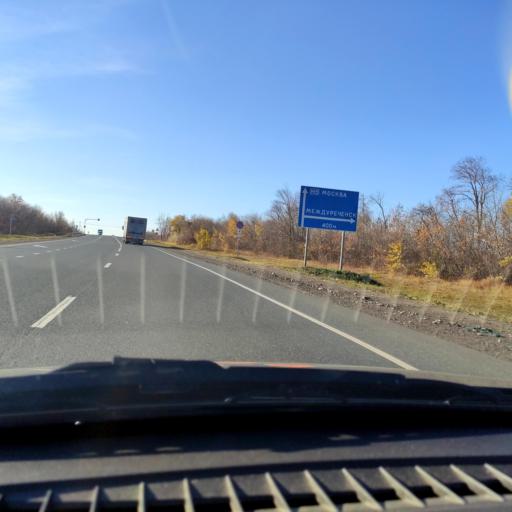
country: RU
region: Samara
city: Mezhdurechensk
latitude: 53.2558
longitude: 49.1351
